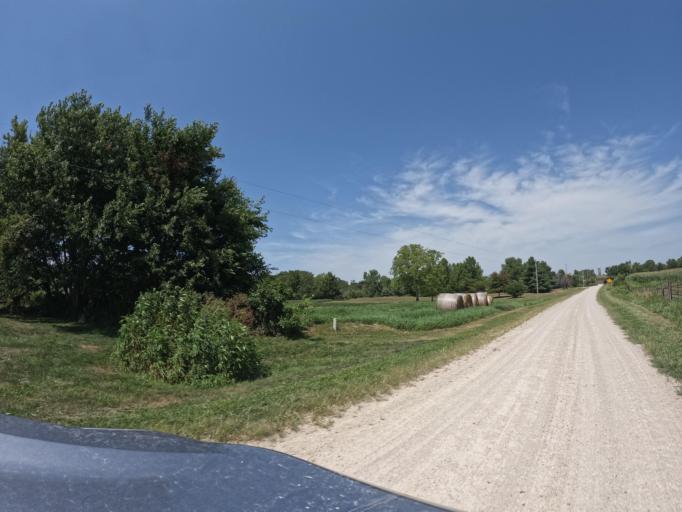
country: US
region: Iowa
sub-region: Henry County
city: Mount Pleasant
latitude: 40.9820
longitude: -91.6532
